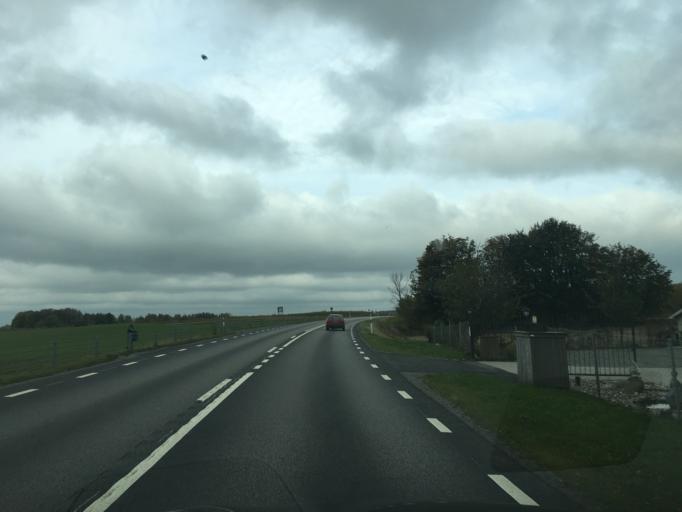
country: SE
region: Skane
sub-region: Tomelilla Kommun
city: Tomelilla
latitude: 55.6394
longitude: 14.0046
